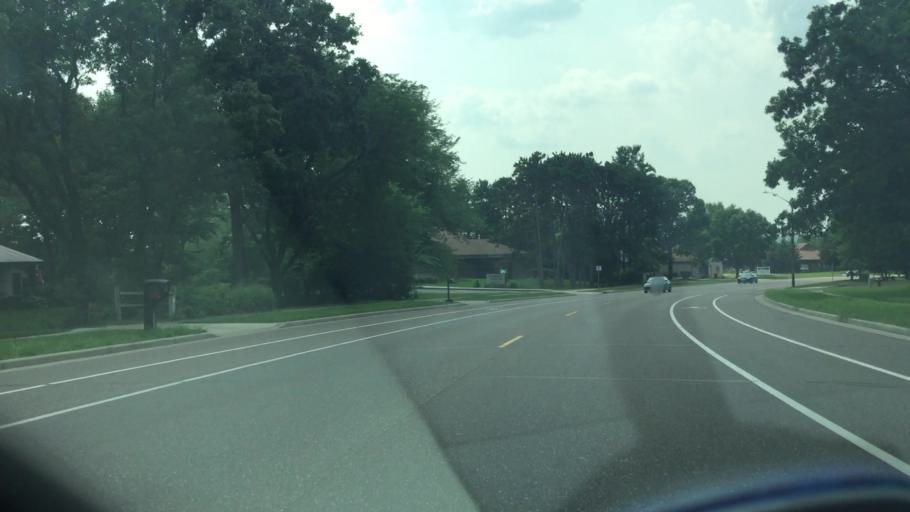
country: US
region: Wisconsin
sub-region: Eau Claire County
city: Altoona
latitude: 44.7690
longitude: -91.4513
